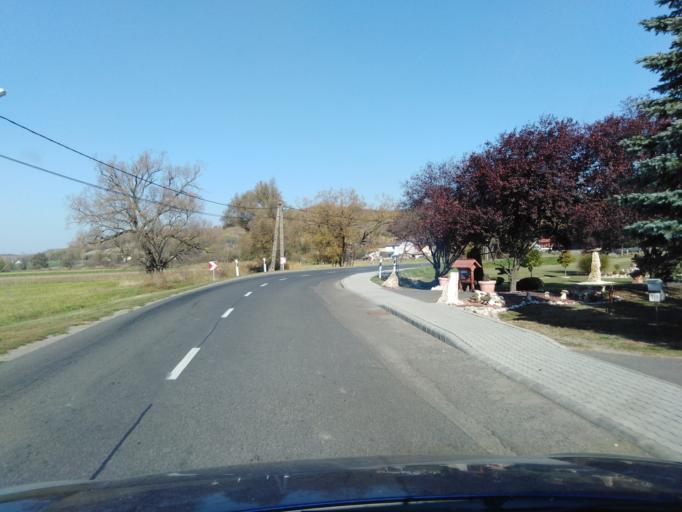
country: HU
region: Nograd
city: Karancskeszi
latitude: 48.1653
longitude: 19.6956
